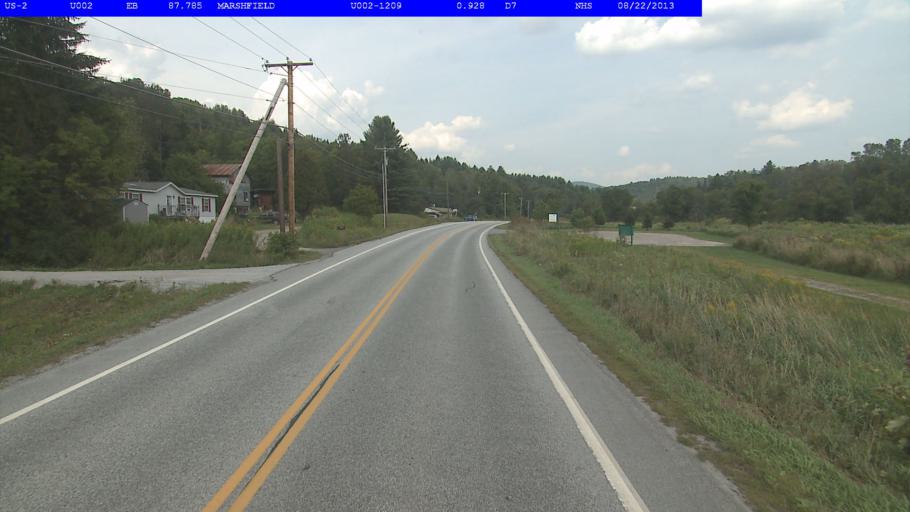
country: US
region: Vermont
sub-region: Washington County
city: Barre
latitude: 44.2882
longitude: -72.4081
